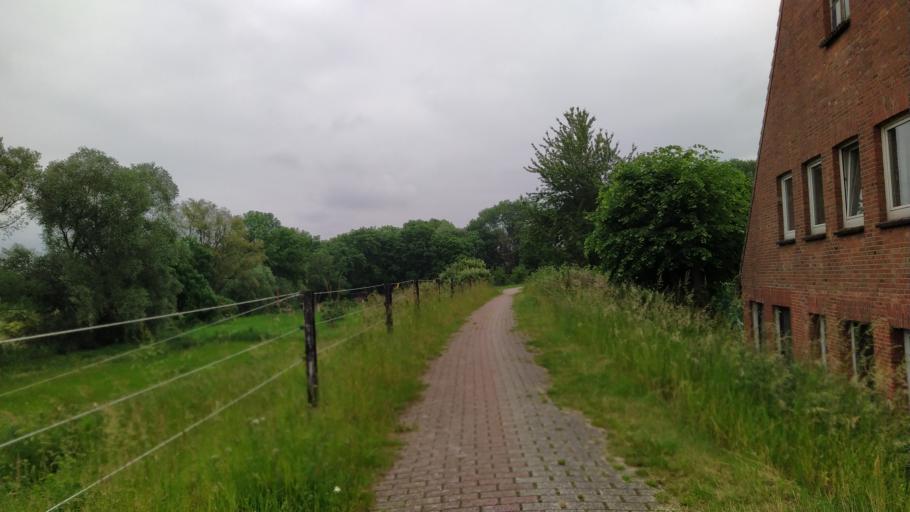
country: DE
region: Hamburg
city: Altona
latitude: 53.4998
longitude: 9.8973
